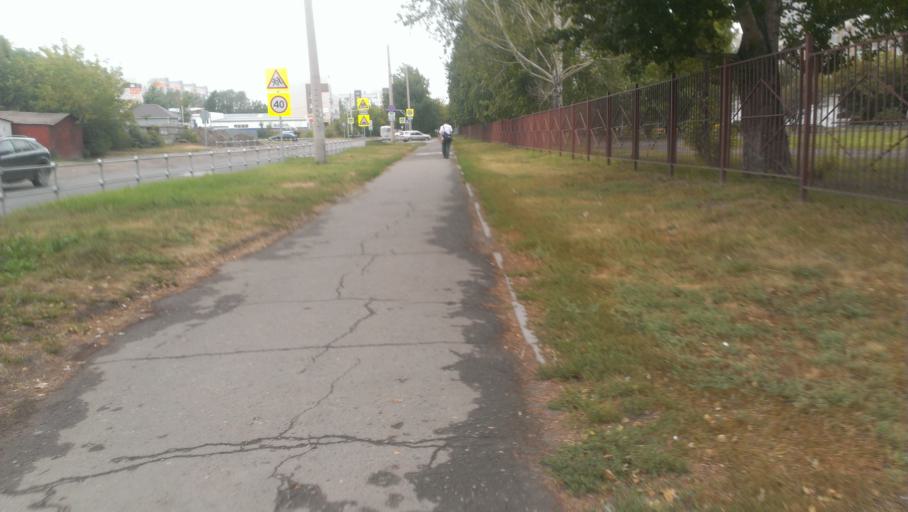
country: RU
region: Altai Krai
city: Novosilikatnyy
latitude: 53.3399
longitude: 83.6673
